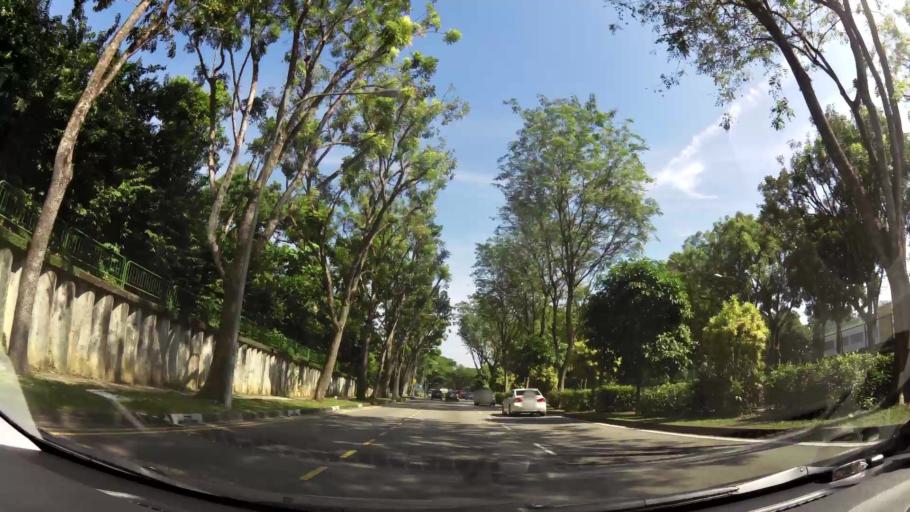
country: SG
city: Singapore
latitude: 1.3663
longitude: 103.8281
